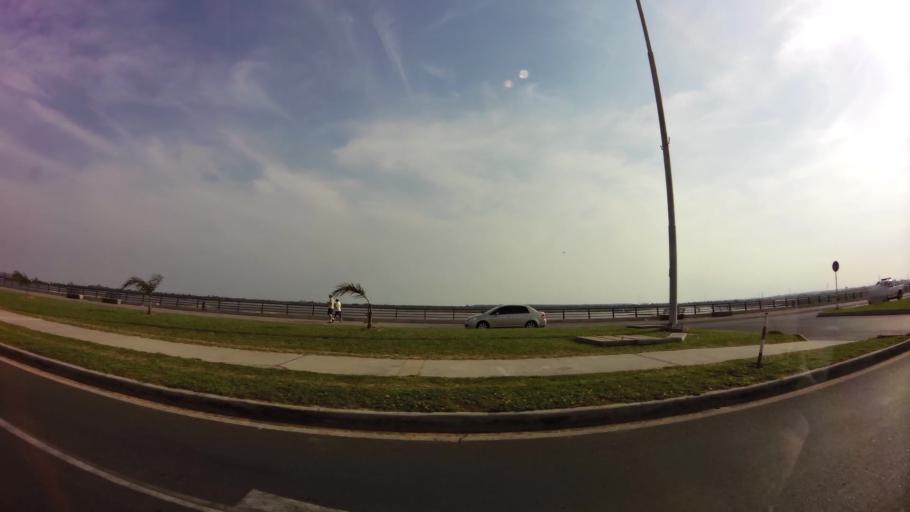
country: PY
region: Asuncion
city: Asuncion
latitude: -25.2765
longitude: -57.6236
